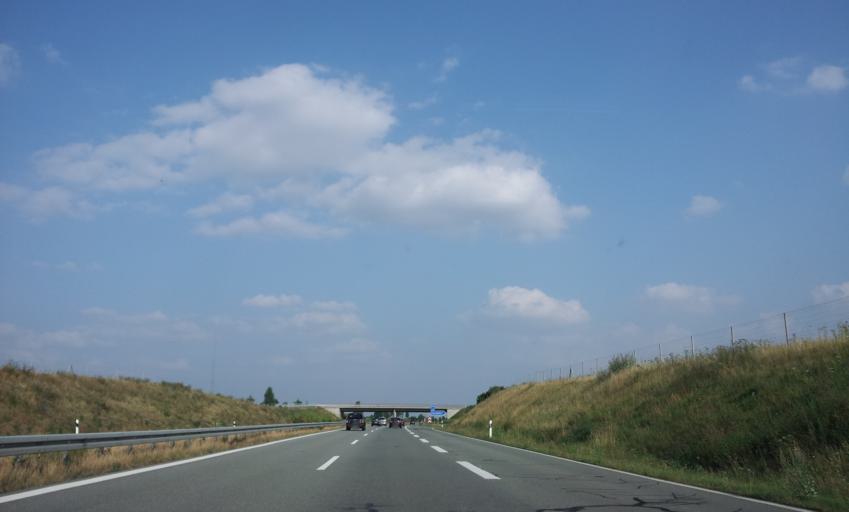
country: DE
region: Mecklenburg-Vorpommern
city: Strasburg
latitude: 53.5457
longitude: 13.7007
